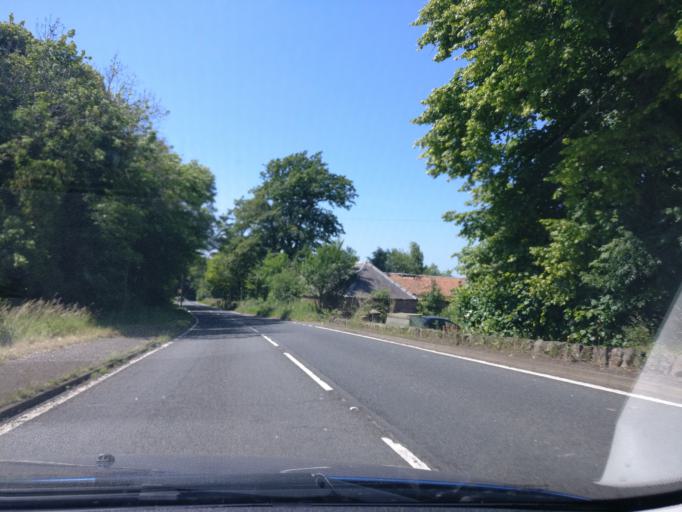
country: GB
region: Scotland
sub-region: East Lothian
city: Longniddry
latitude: 55.9842
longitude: -2.8562
